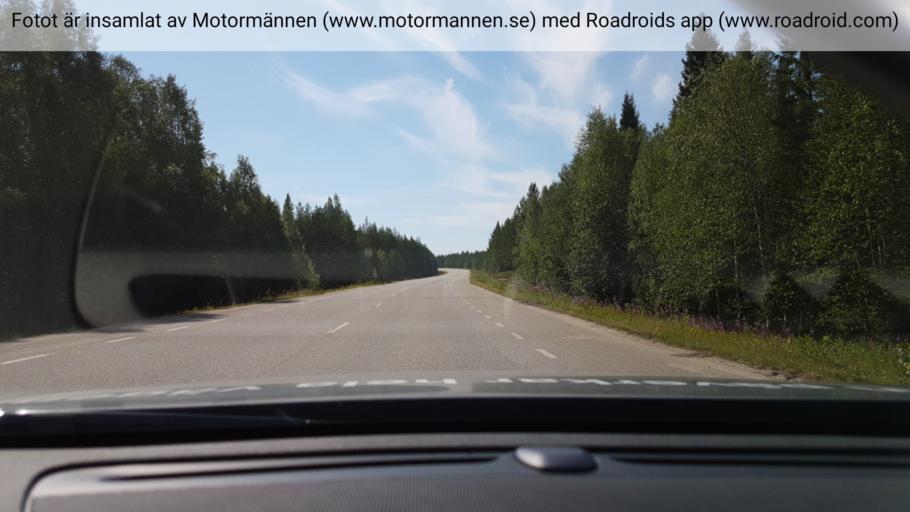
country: SE
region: Vaesterbotten
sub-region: Norsjo Kommun
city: Norsjoe
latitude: 64.5941
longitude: 19.2986
